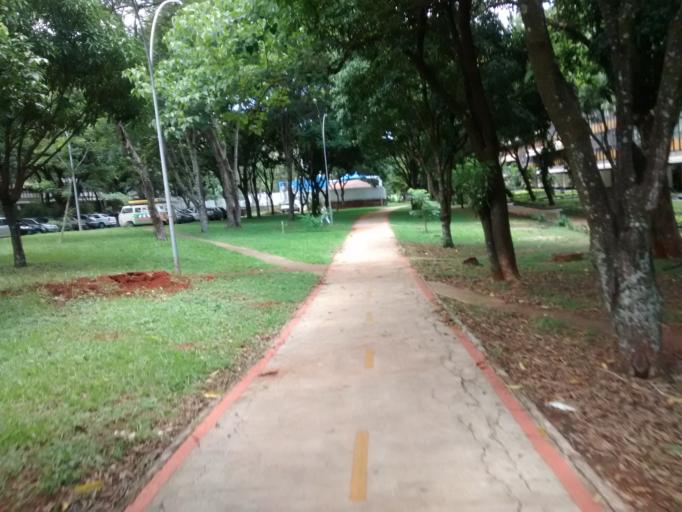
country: BR
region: Federal District
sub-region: Brasilia
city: Brasilia
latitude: -15.7644
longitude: -47.8869
